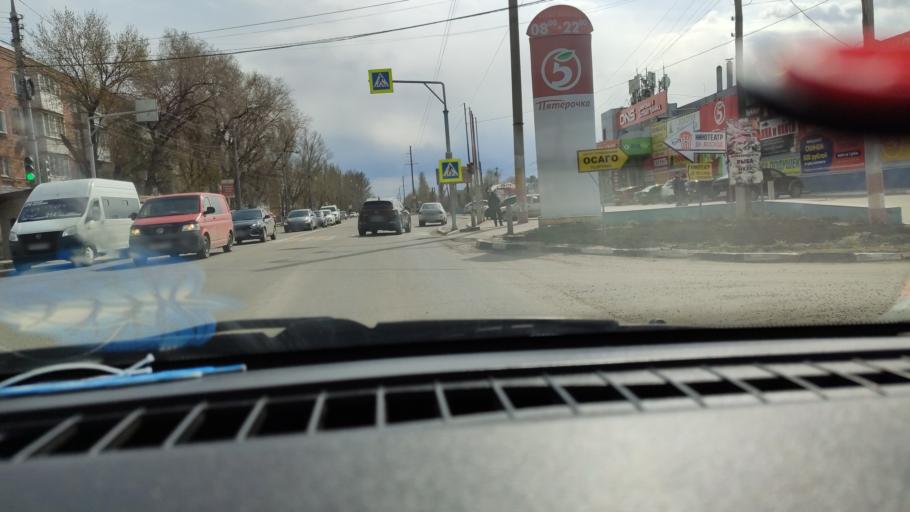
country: RU
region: Saratov
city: Privolzhskiy
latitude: 51.4058
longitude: 46.0390
